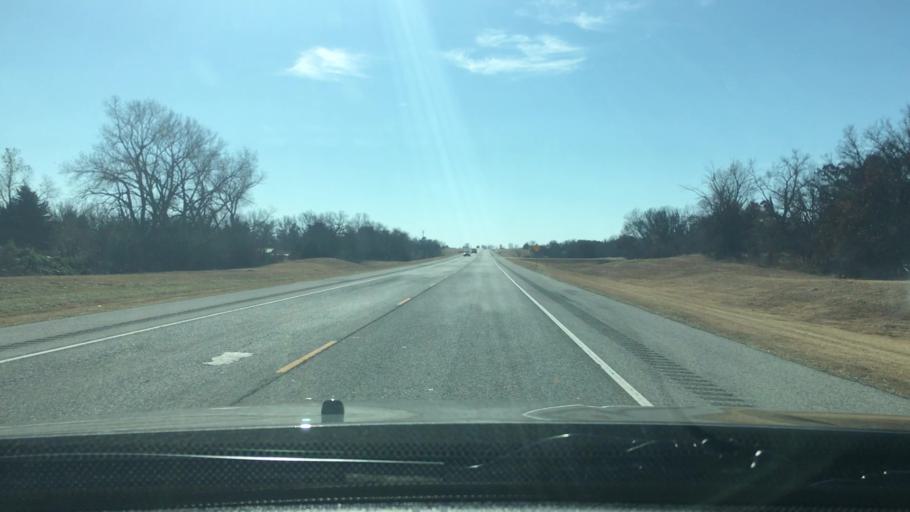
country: US
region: Oklahoma
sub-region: Stephens County
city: Meridian
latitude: 34.4093
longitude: -97.9742
